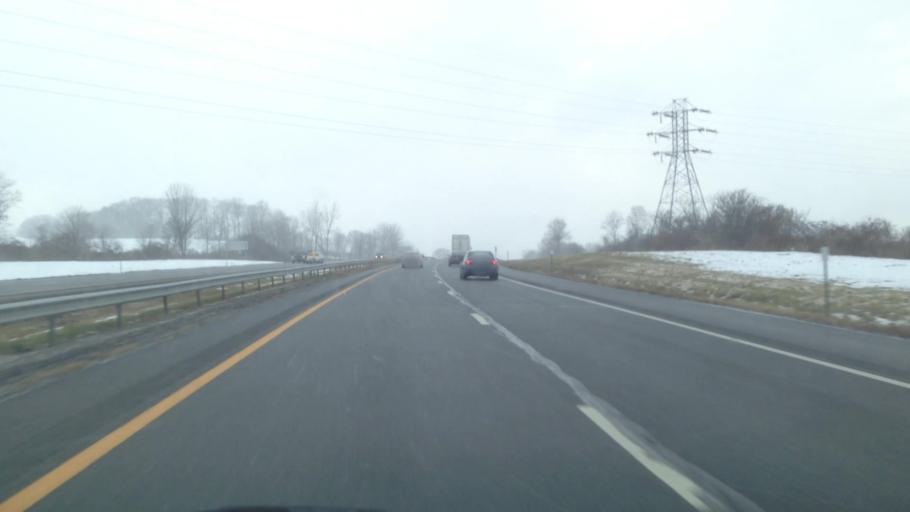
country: US
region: New York
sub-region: Montgomery County
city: Amsterdam
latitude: 42.9037
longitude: -74.1288
